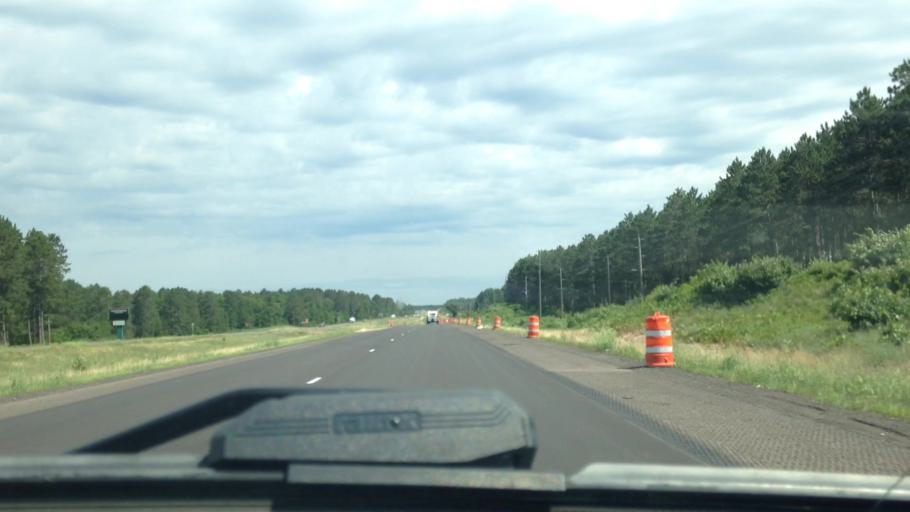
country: US
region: Wisconsin
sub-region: Washburn County
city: Spooner
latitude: 46.1535
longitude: -91.8110
